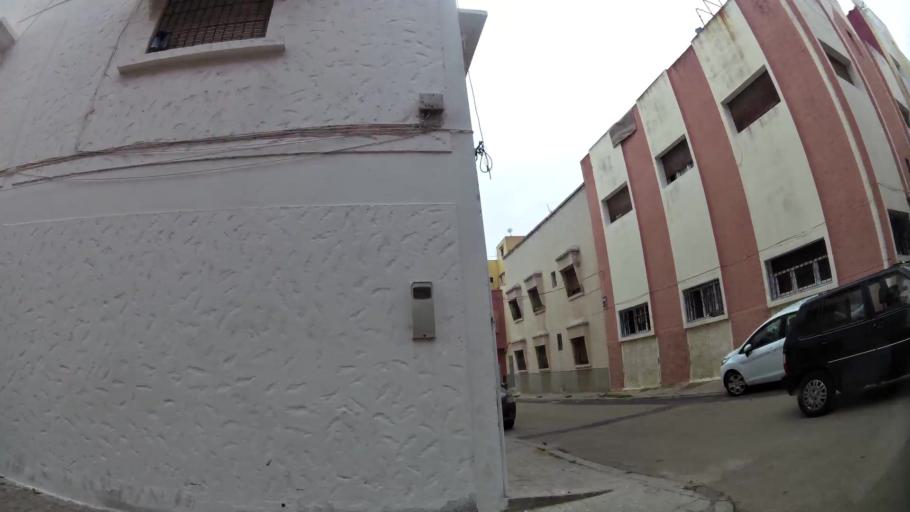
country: MA
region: Rabat-Sale-Zemmour-Zaer
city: Sale
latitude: 34.0302
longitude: -6.8072
